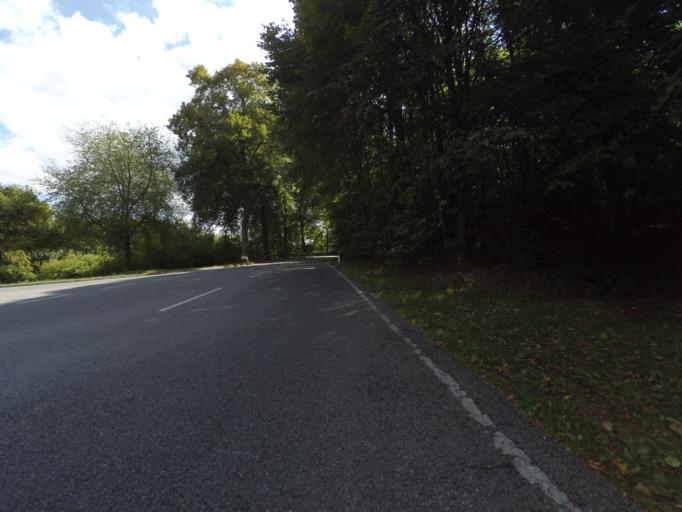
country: LU
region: Luxembourg
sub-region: Canton de Luxembourg
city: Niederanven
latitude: 49.6610
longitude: 6.2288
